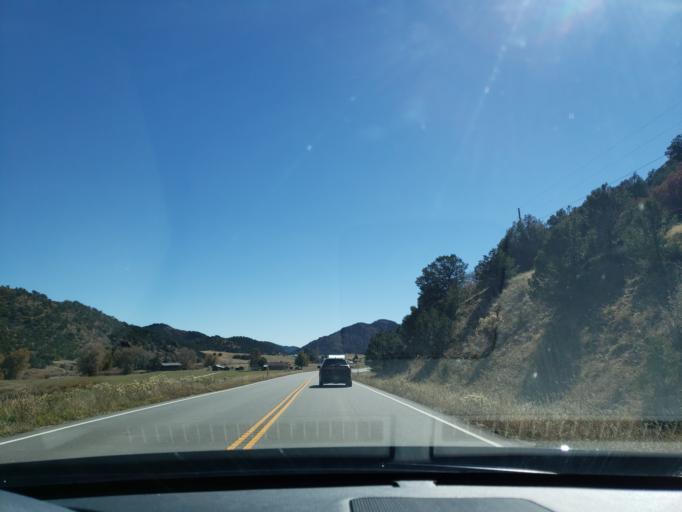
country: US
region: Colorado
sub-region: Fremont County
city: Canon City
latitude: 38.5998
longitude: -105.4290
